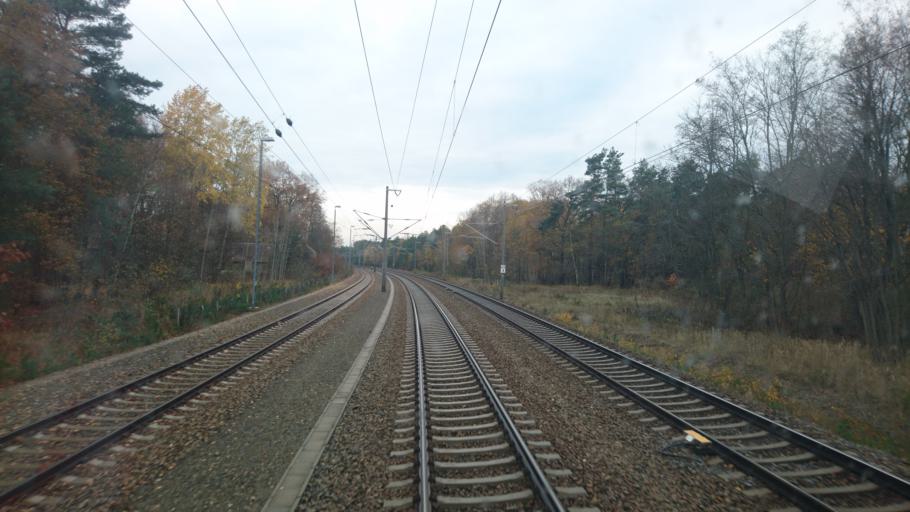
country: DE
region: Saxony
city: Lohsa
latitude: 51.4191
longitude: 14.3364
